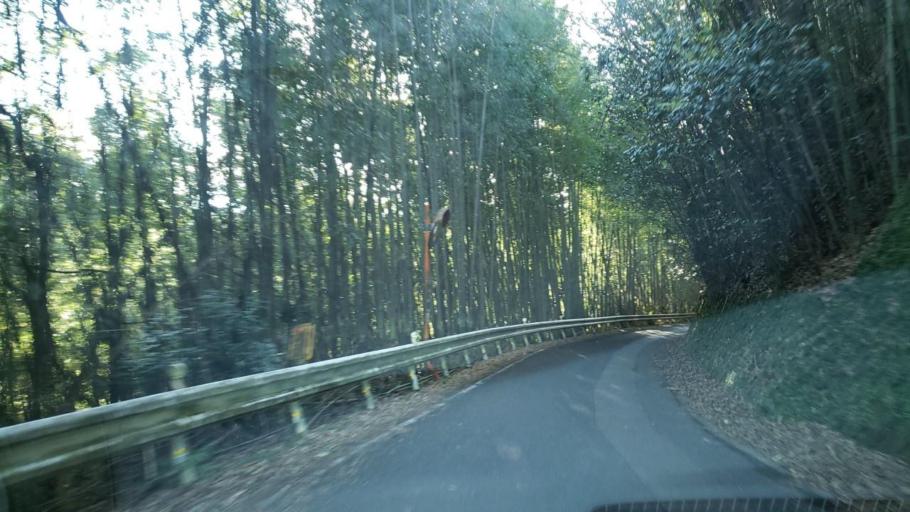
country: JP
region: Tokushima
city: Wakimachi
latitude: 34.0995
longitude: 134.0709
